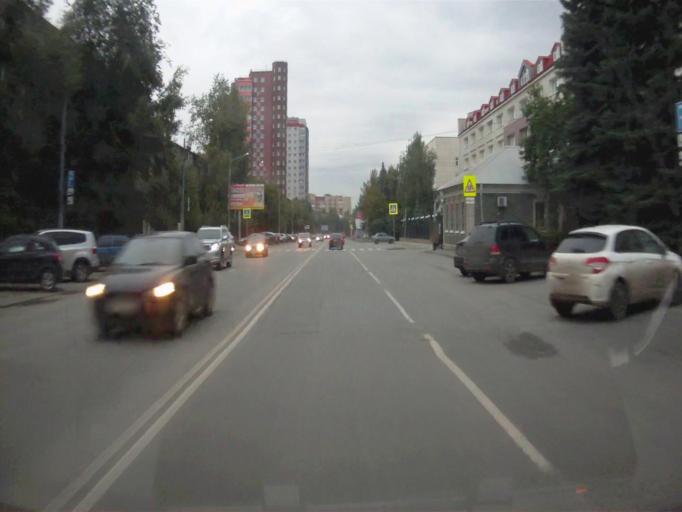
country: RU
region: Chelyabinsk
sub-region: Gorod Chelyabinsk
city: Chelyabinsk
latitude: 55.1495
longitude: 61.3986
